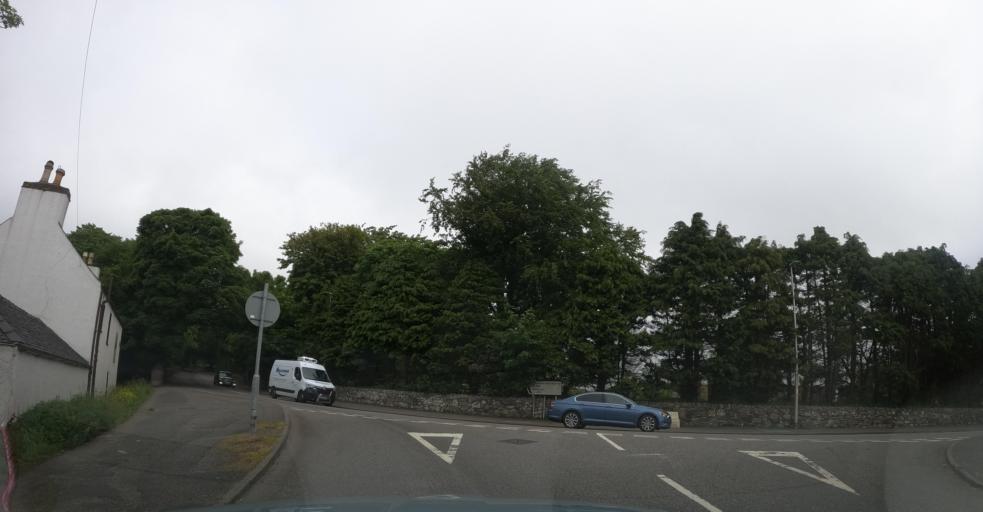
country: GB
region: Scotland
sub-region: Eilean Siar
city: Isle of Lewis
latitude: 58.2187
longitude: -6.3882
